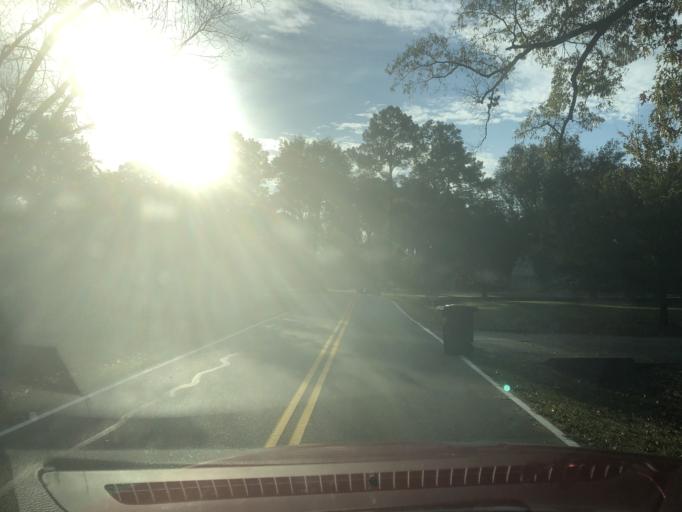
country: US
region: Texas
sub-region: Harris County
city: Spring
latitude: 30.0095
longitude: -95.4740
